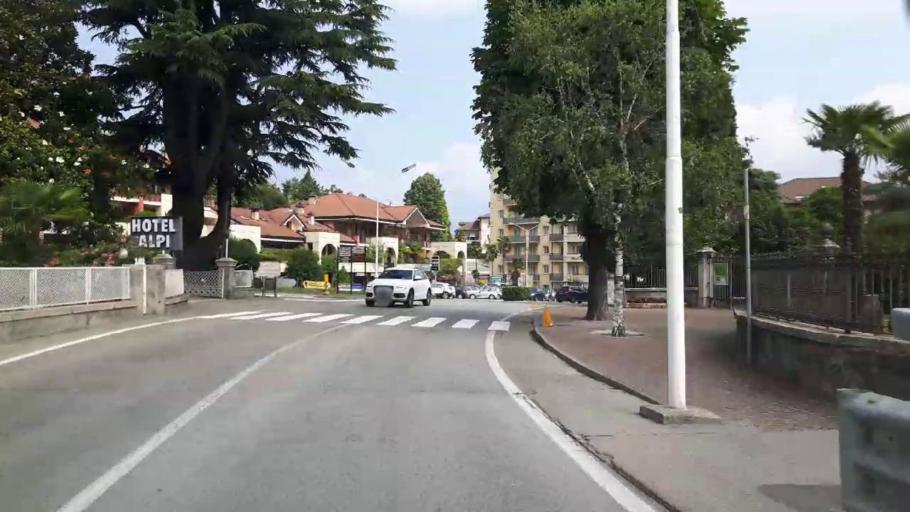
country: IT
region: Piedmont
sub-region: Provincia Verbano-Cusio-Ossola
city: Baveno
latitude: 45.9131
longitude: 8.5019
